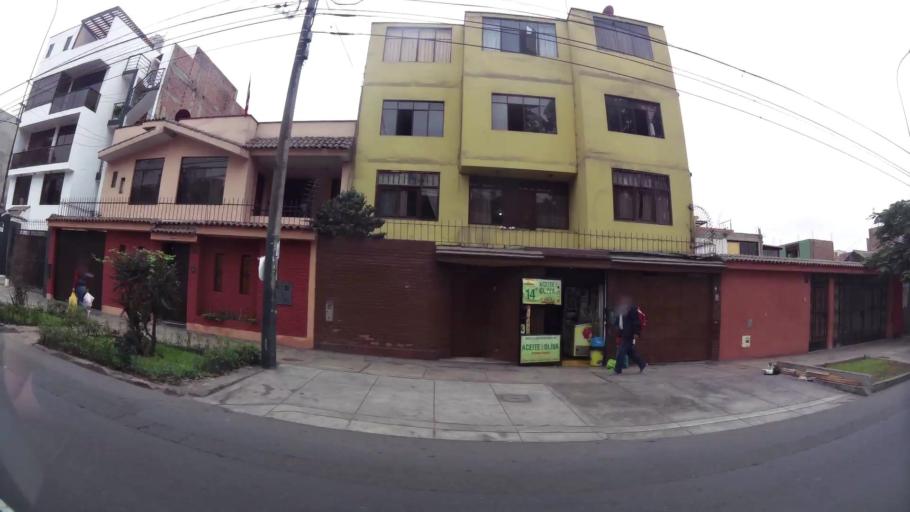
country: PE
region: Lima
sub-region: Lima
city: Surco
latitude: -12.1394
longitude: -76.9844
